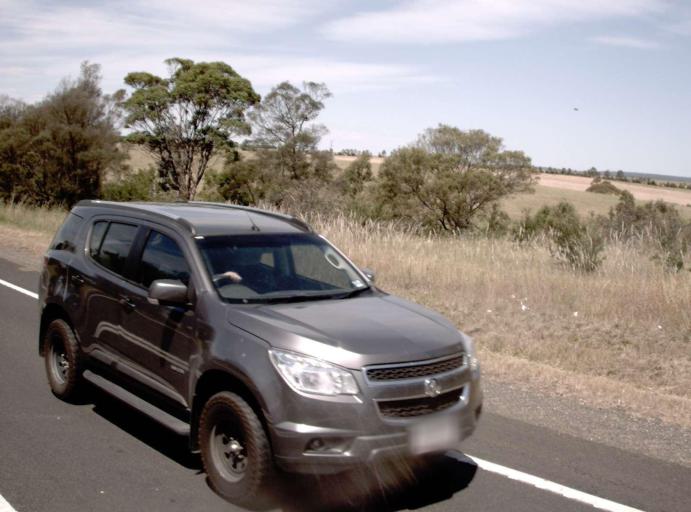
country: AU
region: Victoria
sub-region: Wellington
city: Heyfield
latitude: -38.1312
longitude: 146.8226
